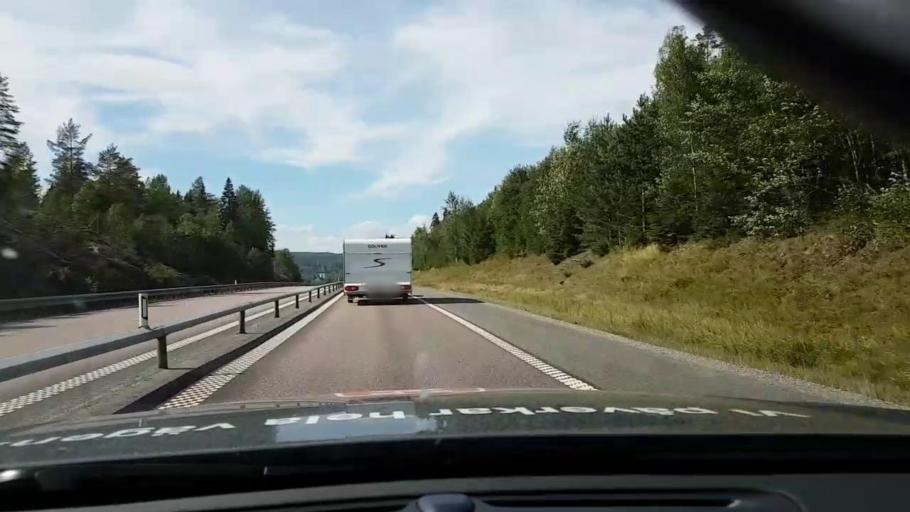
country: SE
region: Vaesternorrland
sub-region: OErnskoeldsviks Kommun
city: Ornskoldsvik
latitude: 63.3142
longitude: 18.8147
